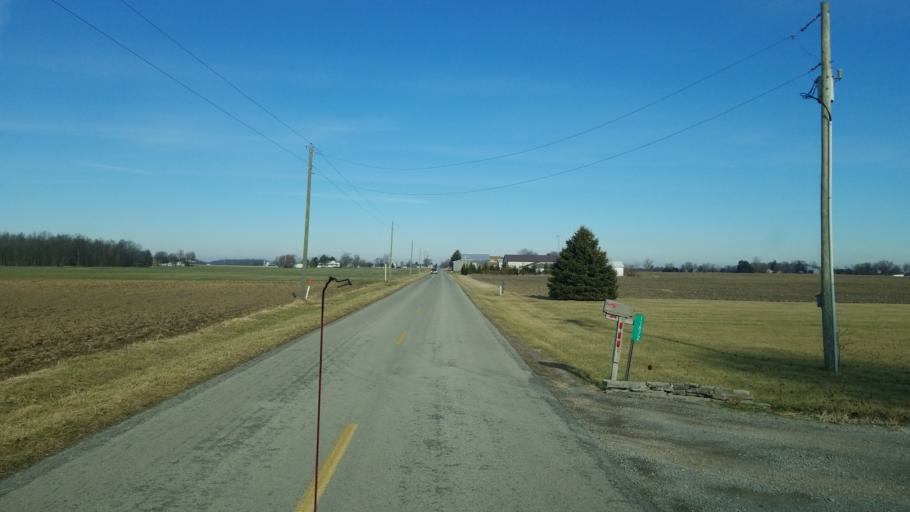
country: US
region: Ohio
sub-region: Putnam County
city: Pandora
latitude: 40.9105
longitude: -83.9377
